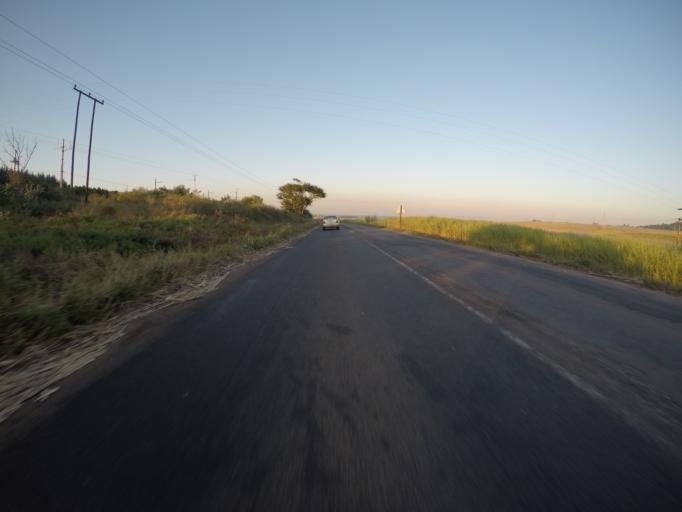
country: ZA
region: KwaZulu-Natal
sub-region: uThungulu District Municipality
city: Empangeni
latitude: -28.8057
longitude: 31.8925
